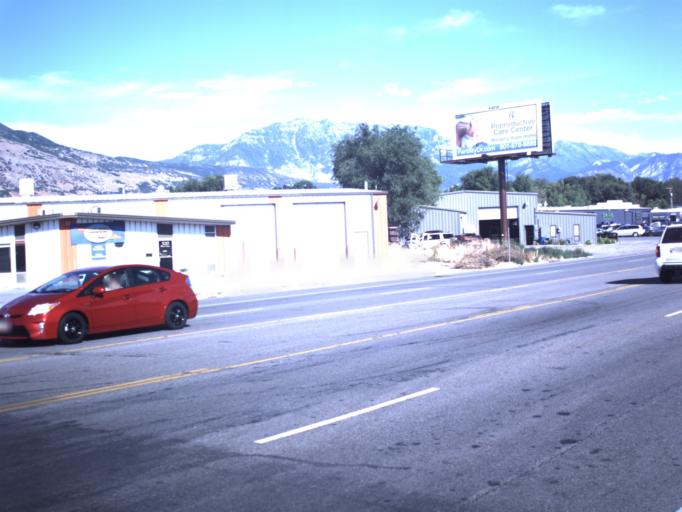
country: US
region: Utah
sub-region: Utah County
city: Pleasant Grove
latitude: 40.3631
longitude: -111.7490
